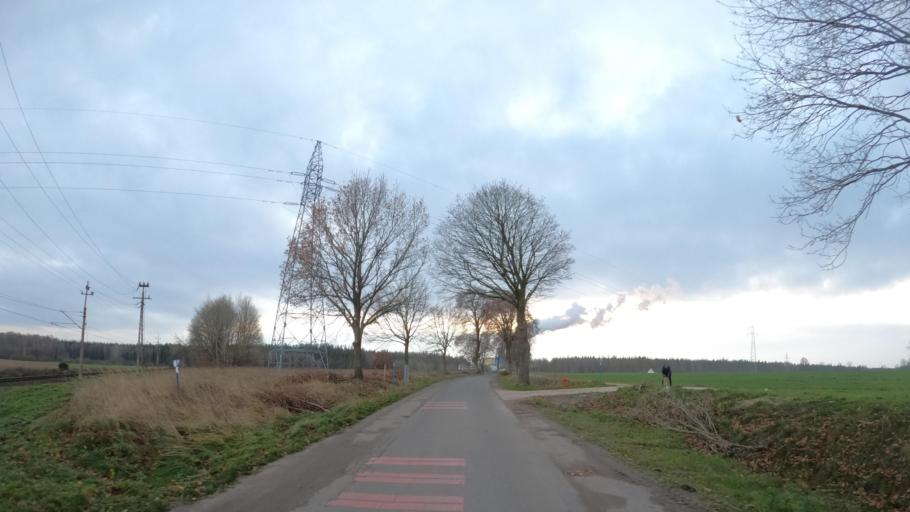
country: PL
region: West Pomeranian Voivodeship
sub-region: Powiat bialogardzki
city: Karlino
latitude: 54.0707
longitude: 15.8771
